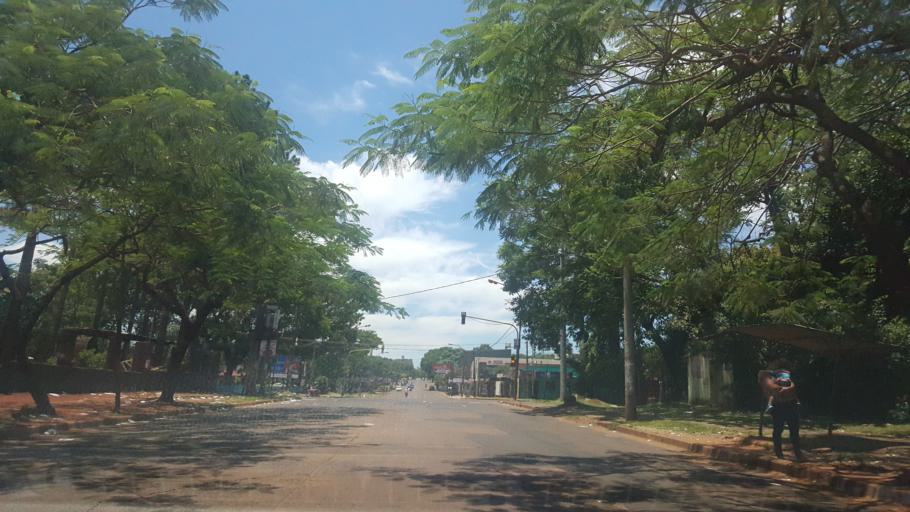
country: AR
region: Misiones
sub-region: Departamento de Capital
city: Posadas
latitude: -27.3672
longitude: -55.9325
